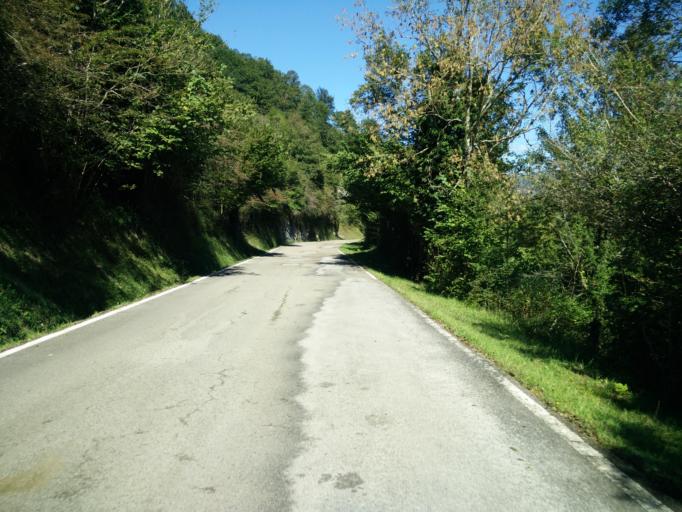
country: ES
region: Cantabria
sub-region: Provincia de Cantabria
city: Ruente
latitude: 43.1320
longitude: -4.2941
